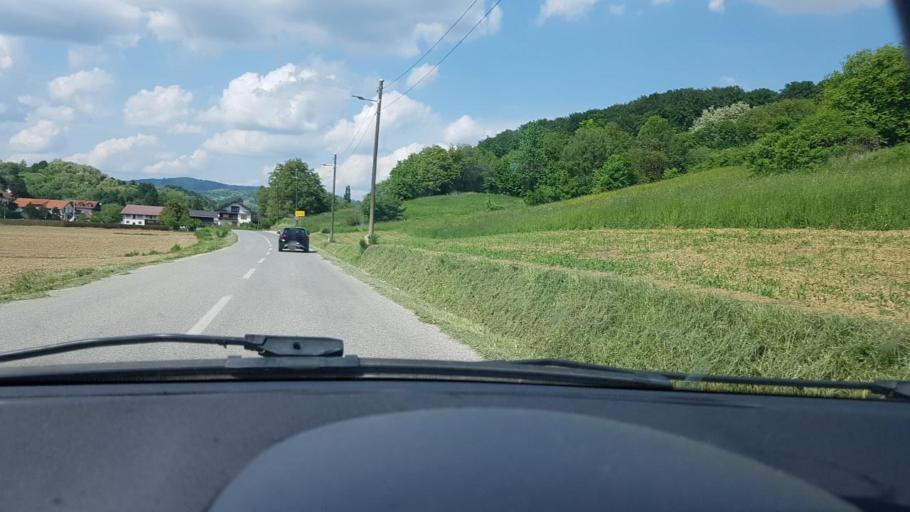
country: HR
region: Grad Zagreb
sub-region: Sesvete
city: Sesvete
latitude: 45.9150
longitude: 16.1695
